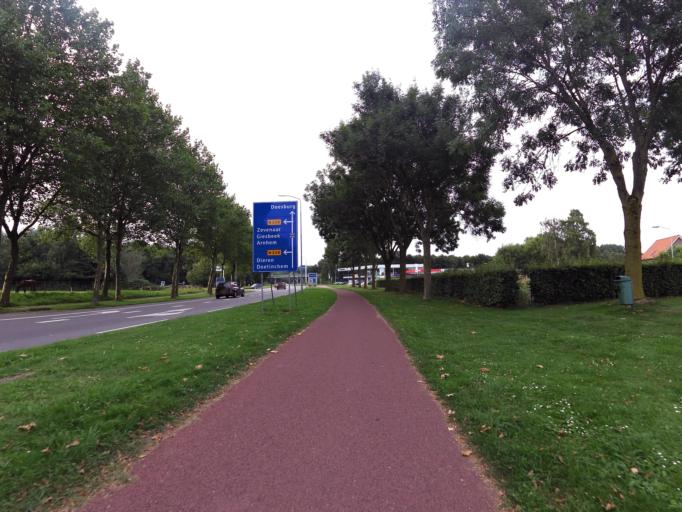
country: NL
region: Gelderland
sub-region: Gemeente Doesburg
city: Doesburg
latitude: 51.9969
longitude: 6.1419
